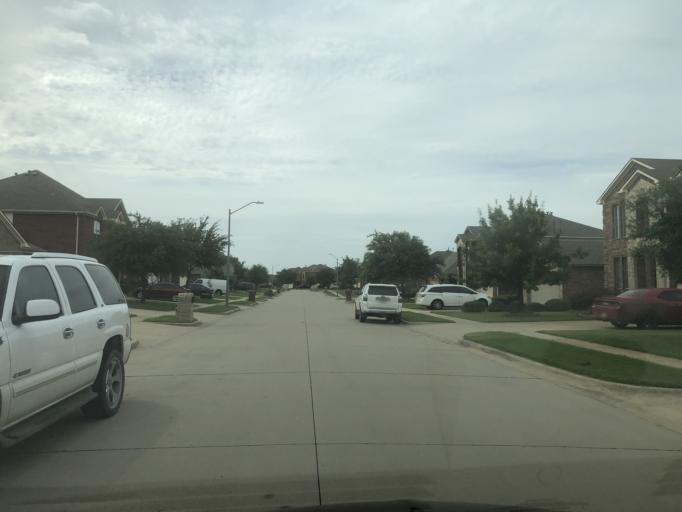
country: US
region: Texas
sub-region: Dallas County
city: Irving
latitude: 32.7966
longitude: -96.9890
